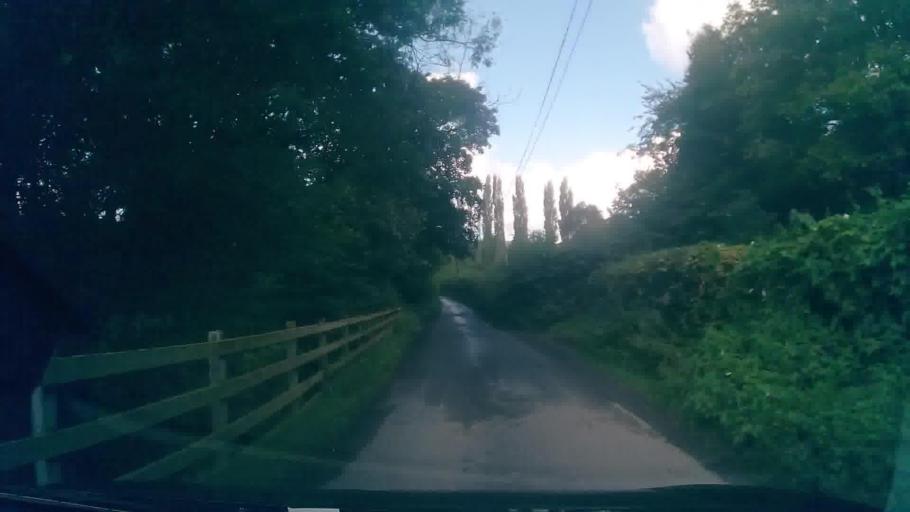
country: GB
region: Wales
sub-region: Sir Powys
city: Llangynog
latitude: 52.8058
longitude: -3.3752
